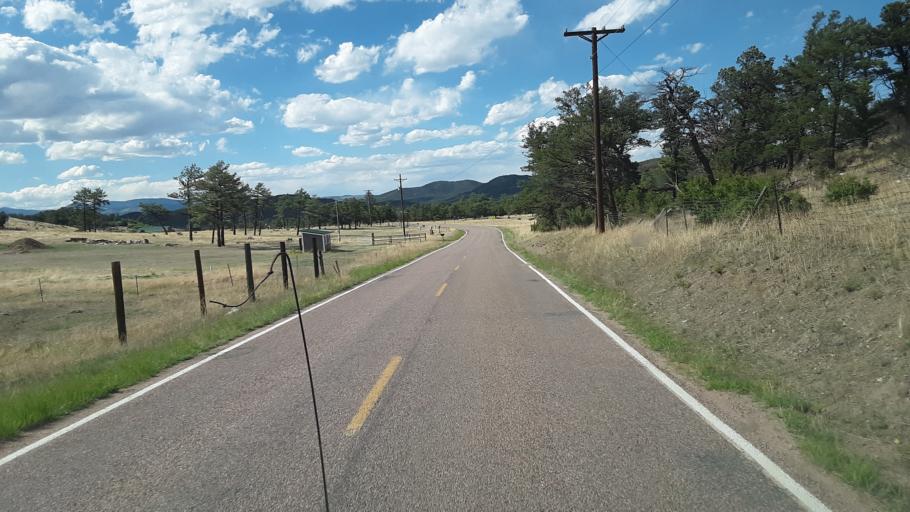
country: US
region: Colorado
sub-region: Custer County
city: Westcliffe
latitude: 38.3330
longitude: -105.4850
